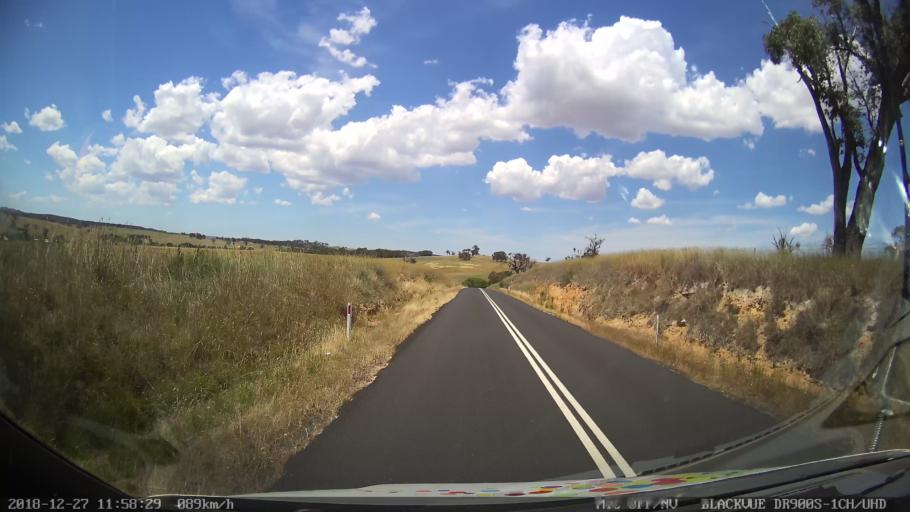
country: AU
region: New South Wales
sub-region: Blayney
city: Blayney
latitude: -33.7245
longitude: 149.3835
